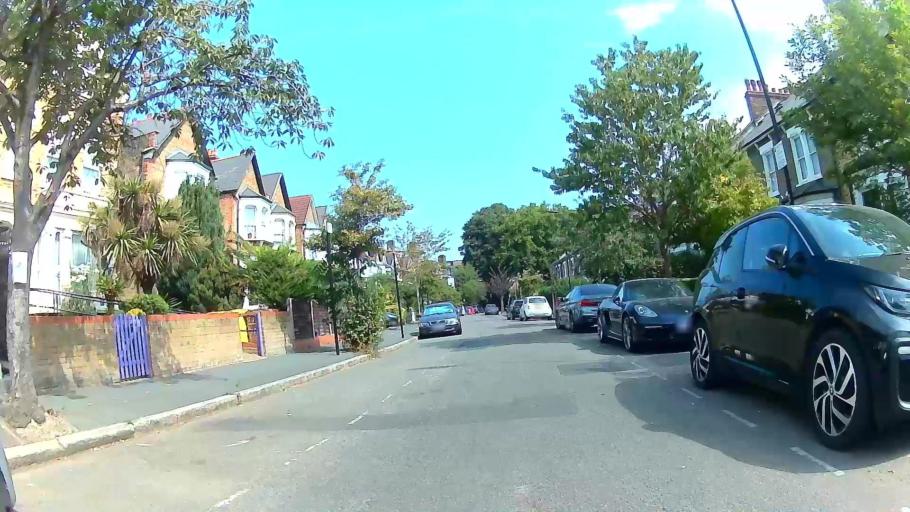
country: GB
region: England
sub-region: Greater London
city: Harringay
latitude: 51.5670
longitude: -0.0878
